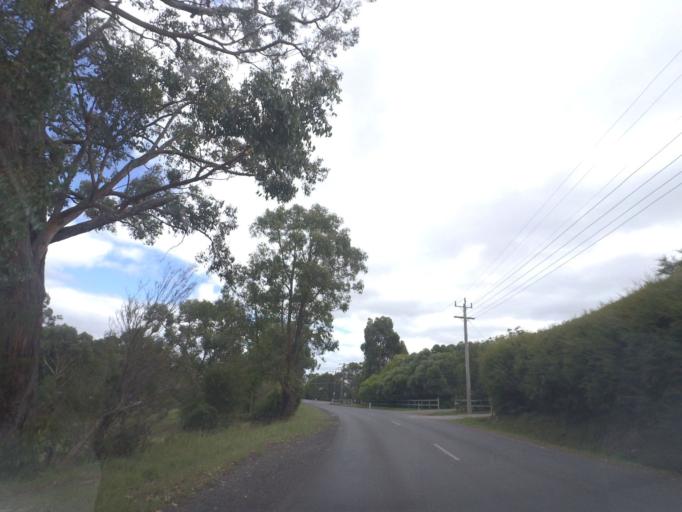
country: AU
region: Victoria
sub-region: Yarra Ranges
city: Woori Yallock
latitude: -37.7890
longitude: 145.5525
